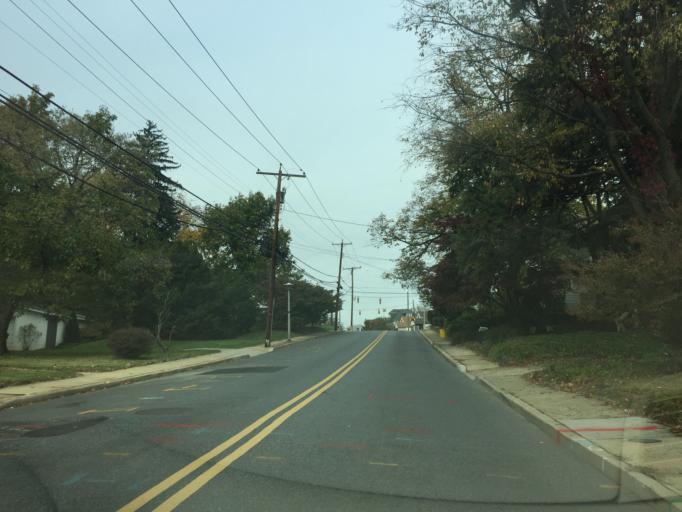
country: US
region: Maryland
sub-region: Baltimore County
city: Parkville
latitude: 39.3481
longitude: -76.5479
